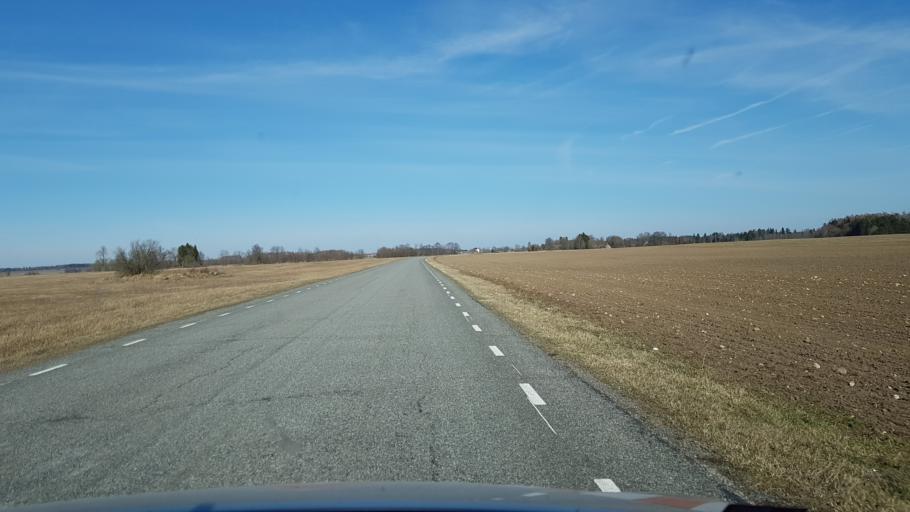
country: EE
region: Laeaene-Virumaa
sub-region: Rakke vald
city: Rakke
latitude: 59.0536
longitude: 26.4311
